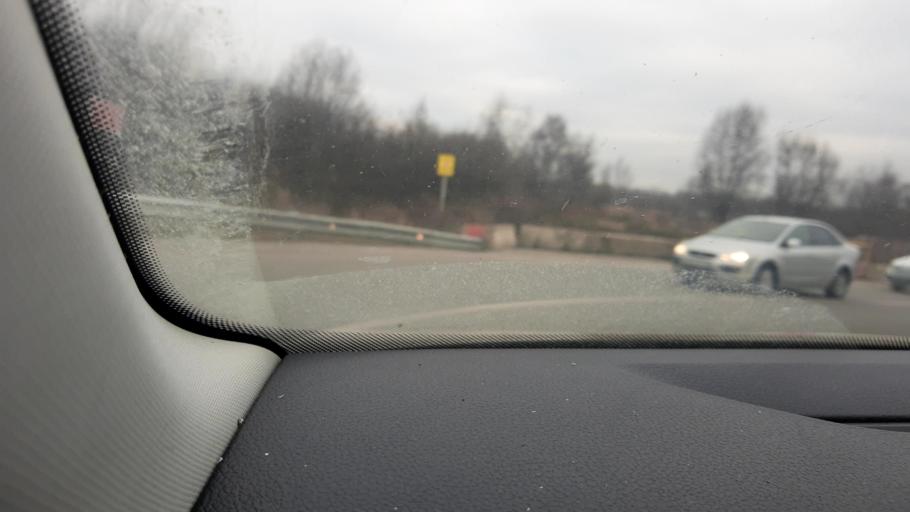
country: RU
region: Moskovskaya
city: Razvilka
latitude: 55.5852
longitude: 37.7152
